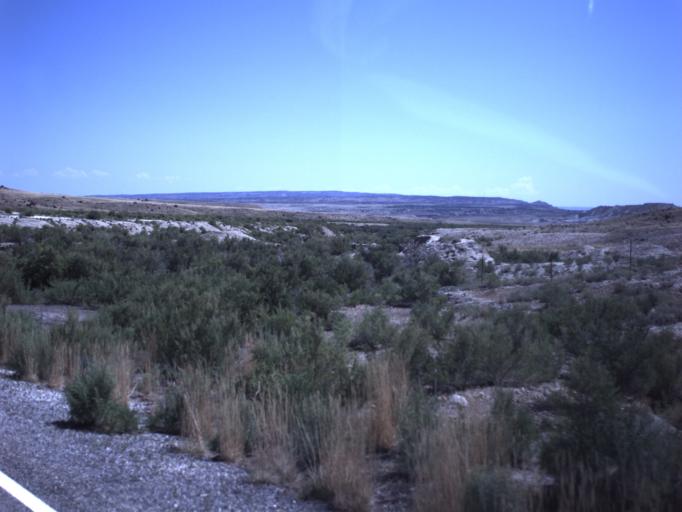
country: US
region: Utah
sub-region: Emery County
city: Ferron
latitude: 38.8029
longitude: -111.3401
